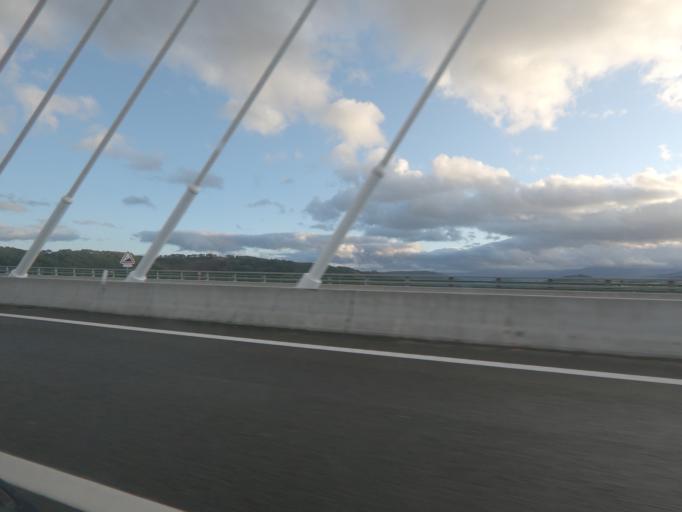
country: PT
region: Vila Real
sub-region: Vila Real
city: Vila Real
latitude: 41.2785
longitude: -7.7487
